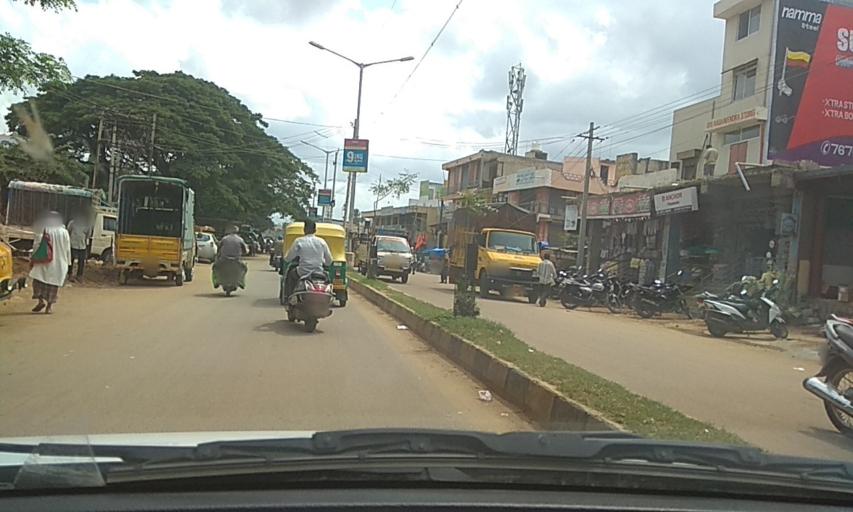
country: IN
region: Karnataka
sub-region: Tumkur
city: Tumkur
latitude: 13.3445
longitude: 77.0993
